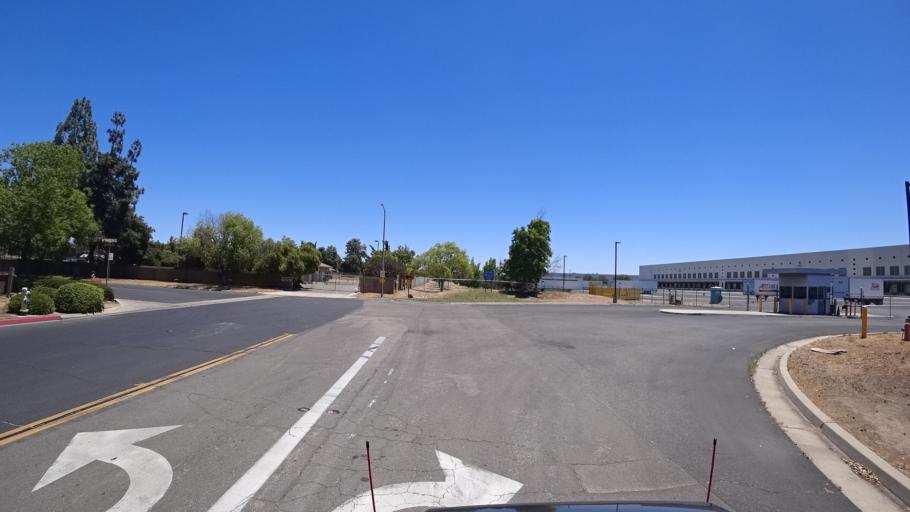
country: US
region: California
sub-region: Fresno County
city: Tarpey Village
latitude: 36.7867
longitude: -119.7113
